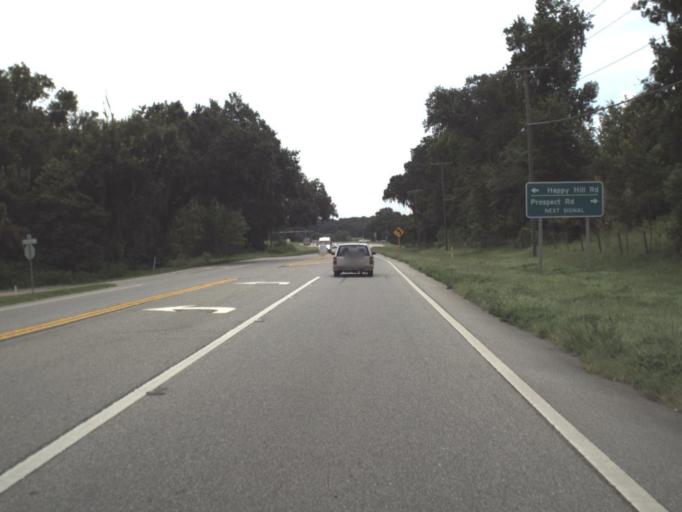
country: US
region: Florida
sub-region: Pasco County
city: Saint Leo
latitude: 28.3356
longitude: -82.2423
